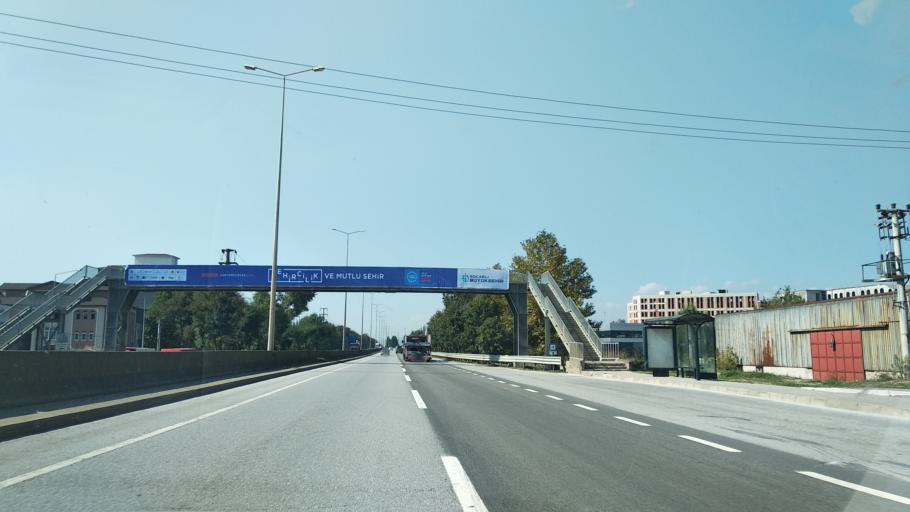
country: TR
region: Kocaeli
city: Kosekoy
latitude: 40.7543
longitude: 30.0177
